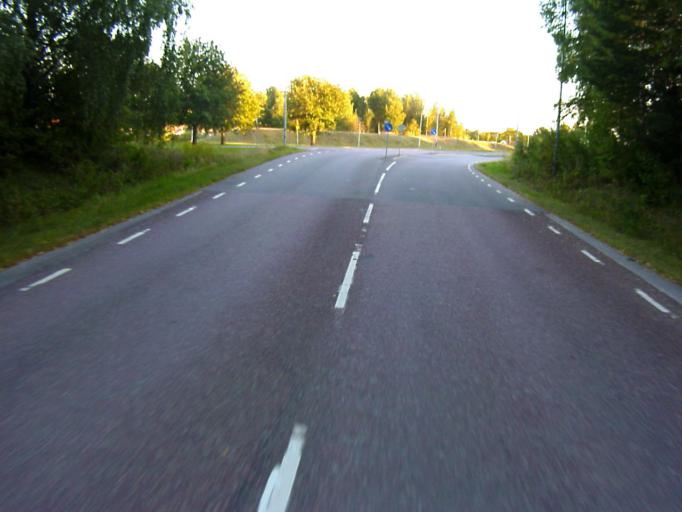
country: SE
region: Soedermanland
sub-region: Eskilstuna Kommun
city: Hallbybrunn
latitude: 59.3491
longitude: 16.4416
